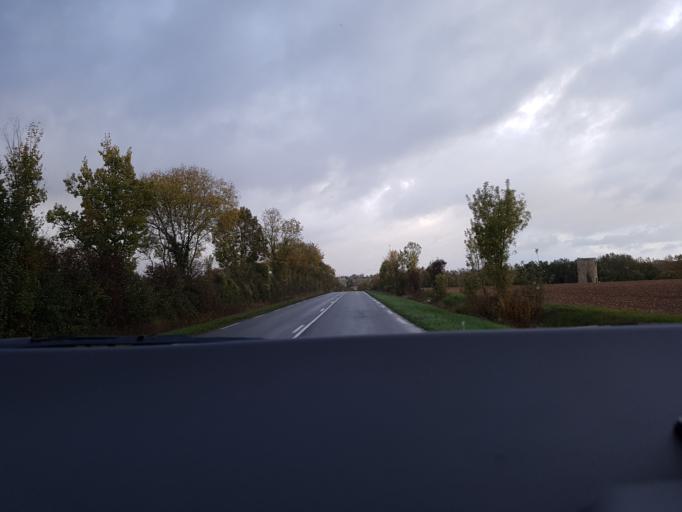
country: FR
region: Poitou-Charentes
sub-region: Departement des Deux-Sevres
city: Brioux-sur-Boutonne
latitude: 46.1767
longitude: -0.1913
